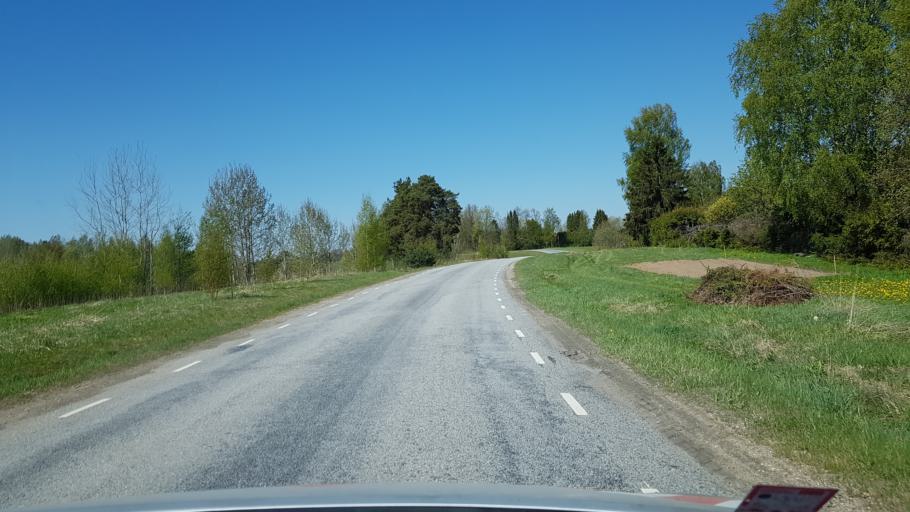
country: EE
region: Vorumaa
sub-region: Voru linn
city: Voru
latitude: 57.9063
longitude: 26.9800
